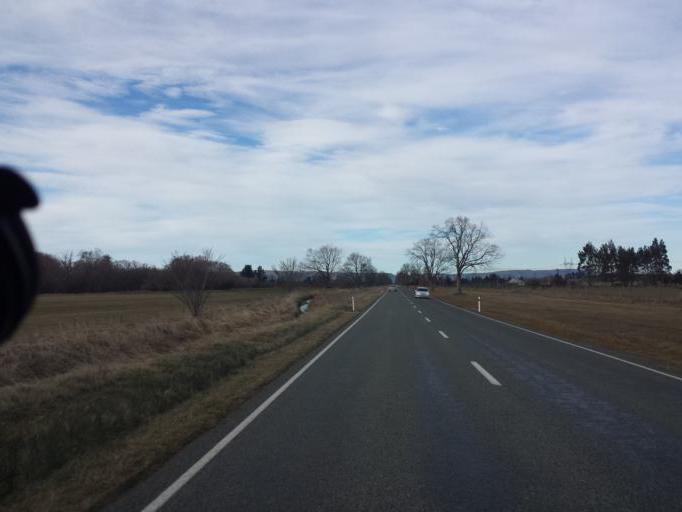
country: NZ
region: Canterbury
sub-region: Timaru District
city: Pleasant Point
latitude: -44.0543
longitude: 170.7691
